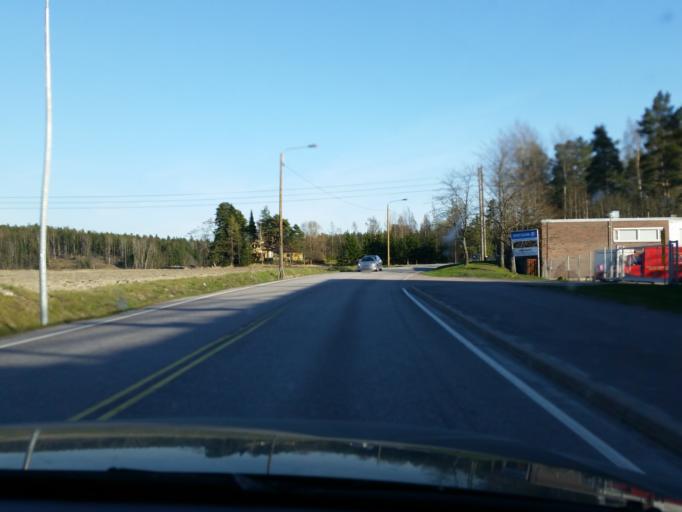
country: FI
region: Uusimaa
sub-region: Helsinki
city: Kirkkonummi
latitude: 60.1309
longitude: 24.5152
